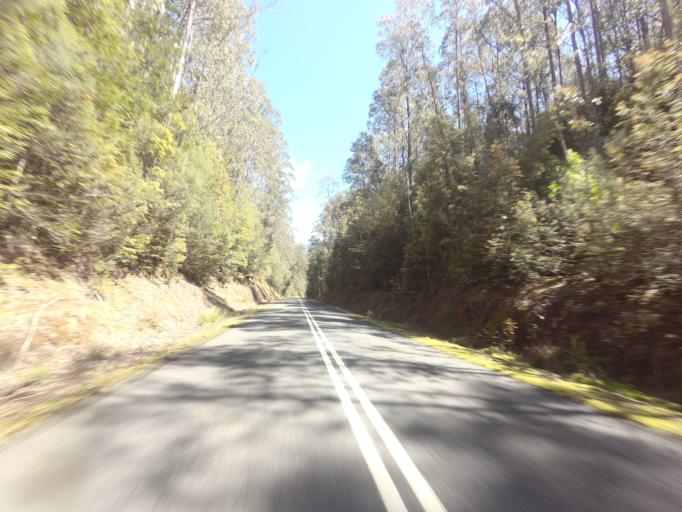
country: AU
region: Tasmania
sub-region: Huon Valley
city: Geeveston
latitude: -42.8208
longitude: 146.2992
